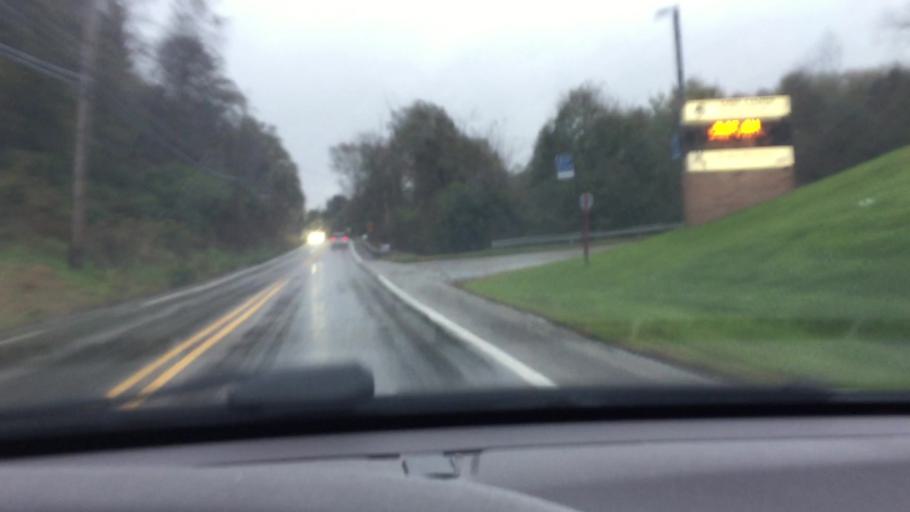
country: US
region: Pennsylvania
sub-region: Allegheny County
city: Pleasant Hills
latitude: 40.3245
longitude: -79.9399
